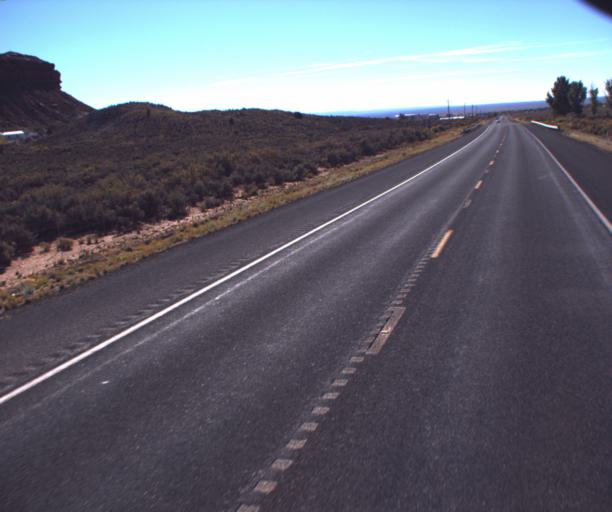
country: US
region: Arizona
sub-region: Coconino County
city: Fredonia
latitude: 36.9817
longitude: -112.5294
